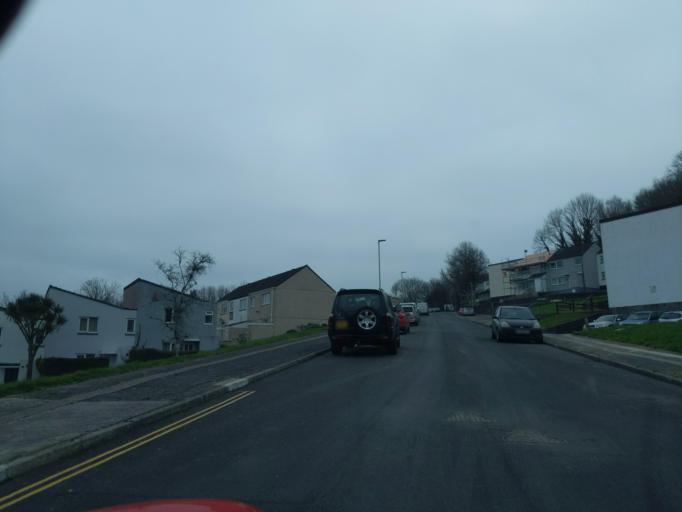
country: GB
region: England
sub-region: Plymouth
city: Plymstock
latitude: 50.3941
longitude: -4.1017
